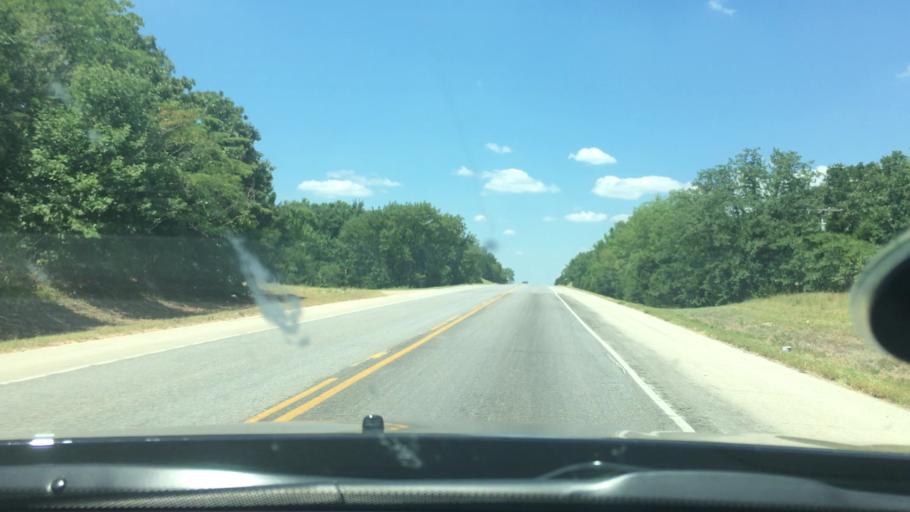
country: US
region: Oklahoma
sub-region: Carter County
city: Dickson
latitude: 34.1873
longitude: -96.9243
